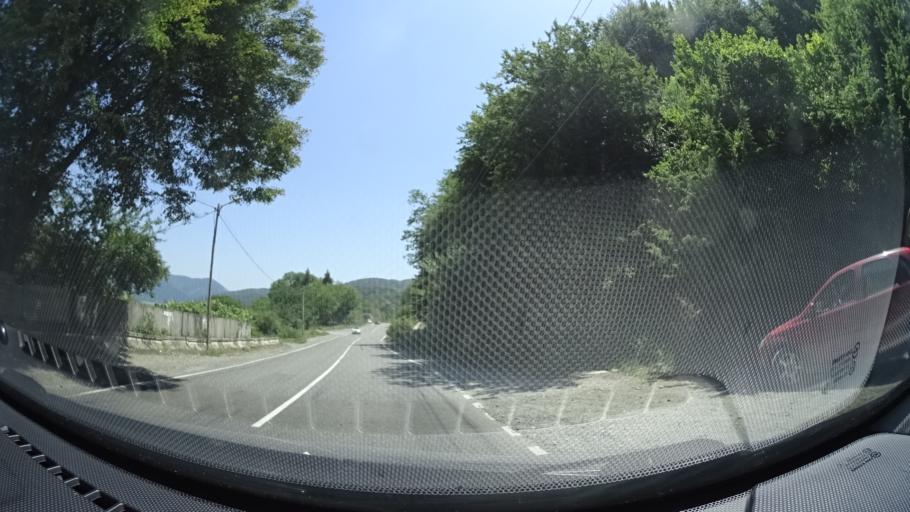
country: GE
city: Zhinvali
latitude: 42.1695
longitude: 44.6951
